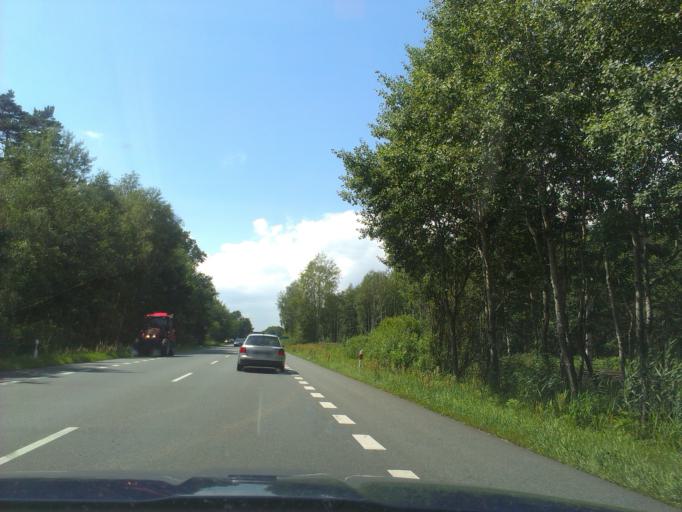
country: PL
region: West Pomeranian Voivodeship
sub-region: Powiat kamienski
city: Miedzyzdroje
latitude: 53.8999
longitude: 14.3678
